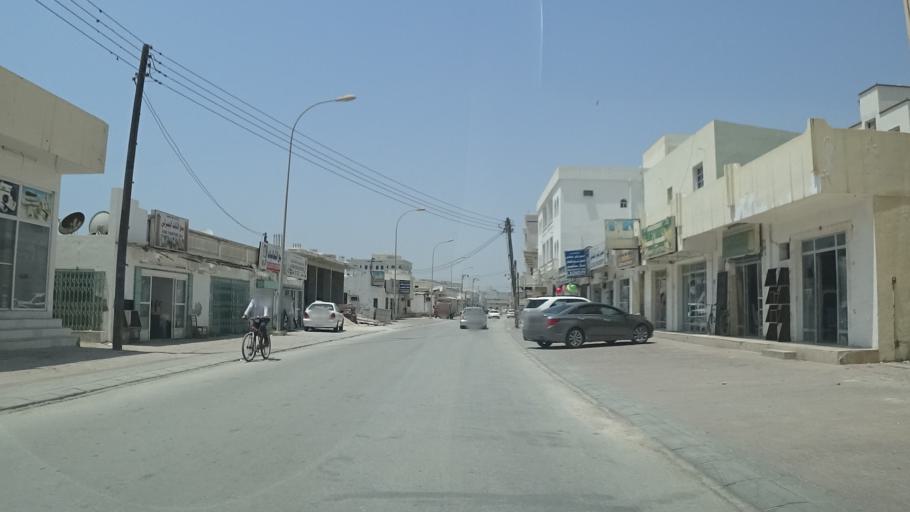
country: OM
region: Zufar
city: Salalah
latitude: 17.0153
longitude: 54.1117
